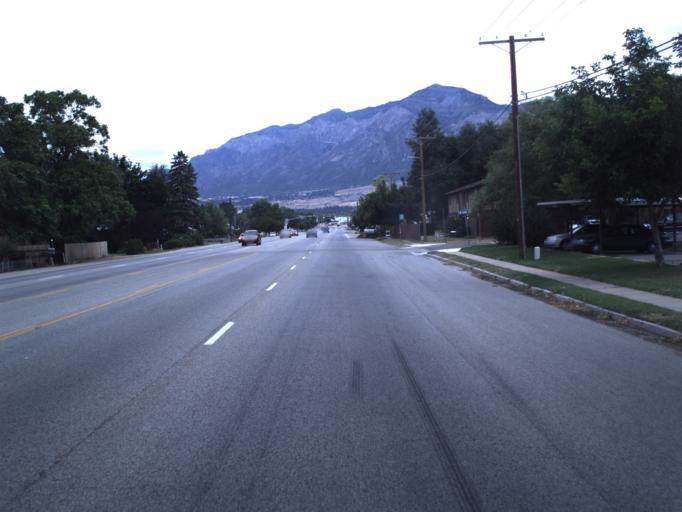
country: US
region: Utah
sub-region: Weber County
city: Harrisville
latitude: 41.2635
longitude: -111.9777
